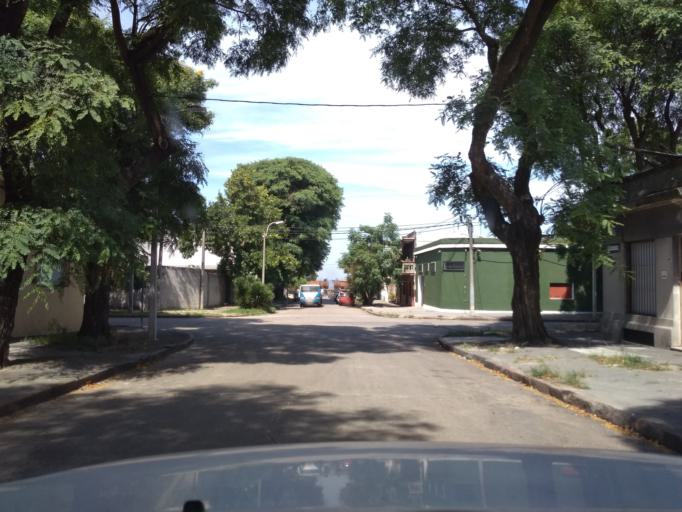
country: UY
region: Montevideo
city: Montevideo
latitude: -34.8779
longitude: -56.2010
